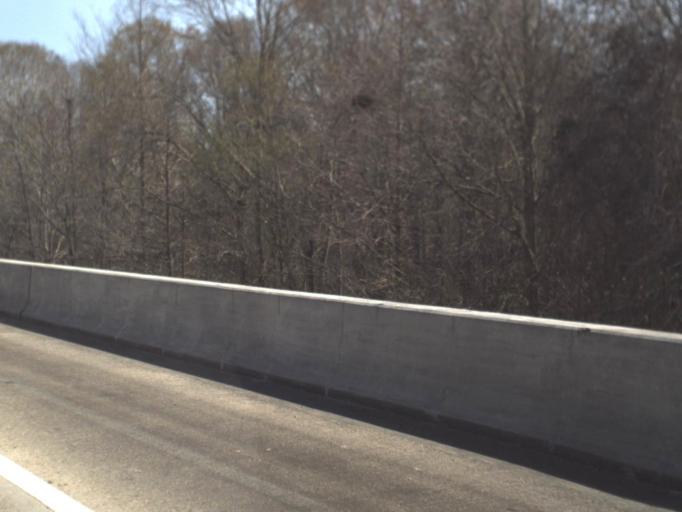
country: US
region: Florida
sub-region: Holmes County
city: Bonifay
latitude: 30.7555
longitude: -85.6191
